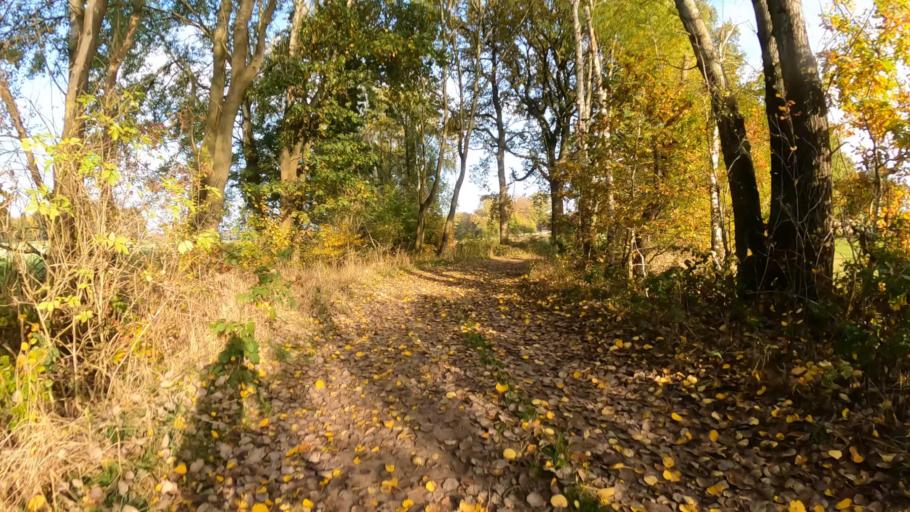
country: DE
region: Lower Saxony
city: Buchholz in der Nordheide
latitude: 53.3371
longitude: 9.8306
